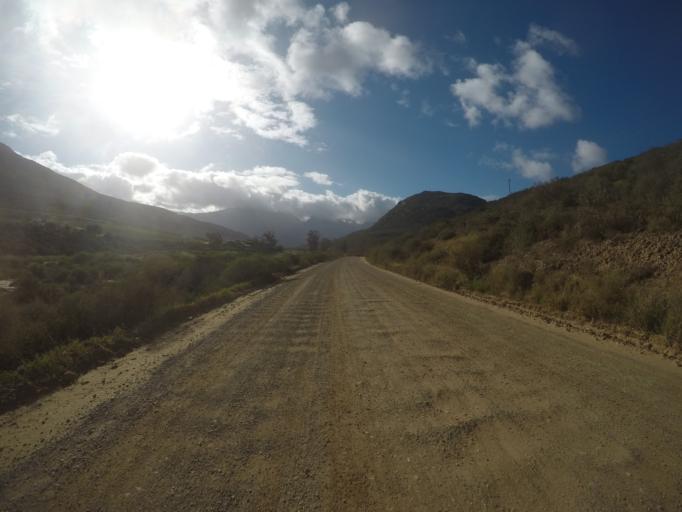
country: ZA
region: Western Cape
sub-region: West Coast District Municipality
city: Clanwilliam
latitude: -32.3650
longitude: 18.9503
